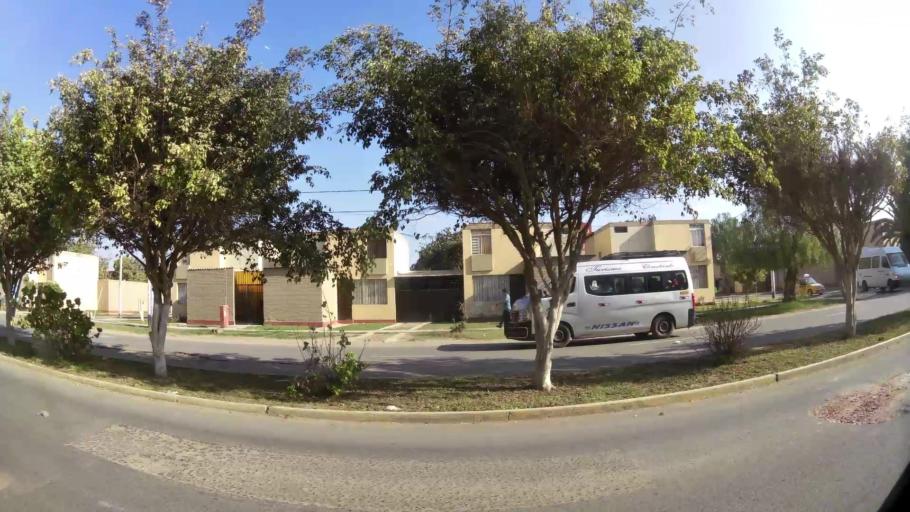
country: PE
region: Lambayeque
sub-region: Provincia de Chiclayo
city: Chiclayo
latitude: -6.7658
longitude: -79.8505
